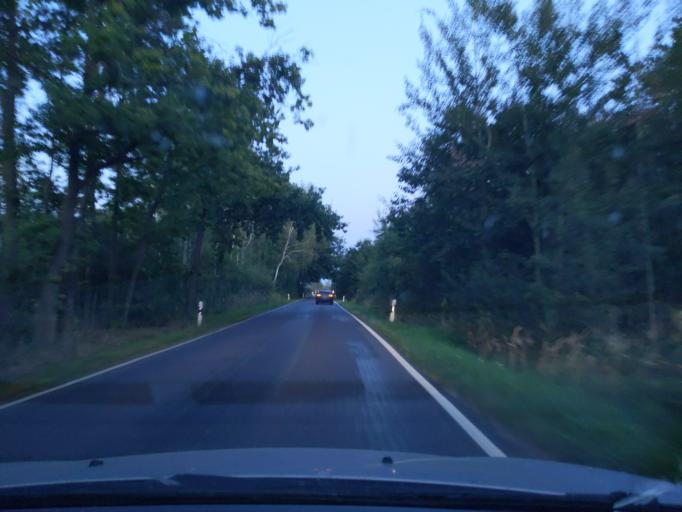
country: DE
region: Saxony
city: Konigswartha
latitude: 51.3447
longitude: 14.3595
